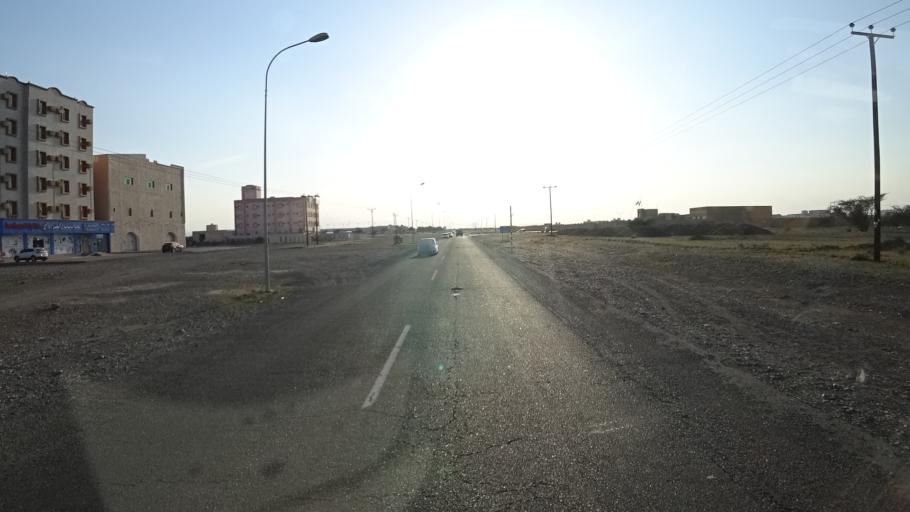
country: OM
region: Al Batinah
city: Al Khaburah
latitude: 23.9504
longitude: 57.0572
